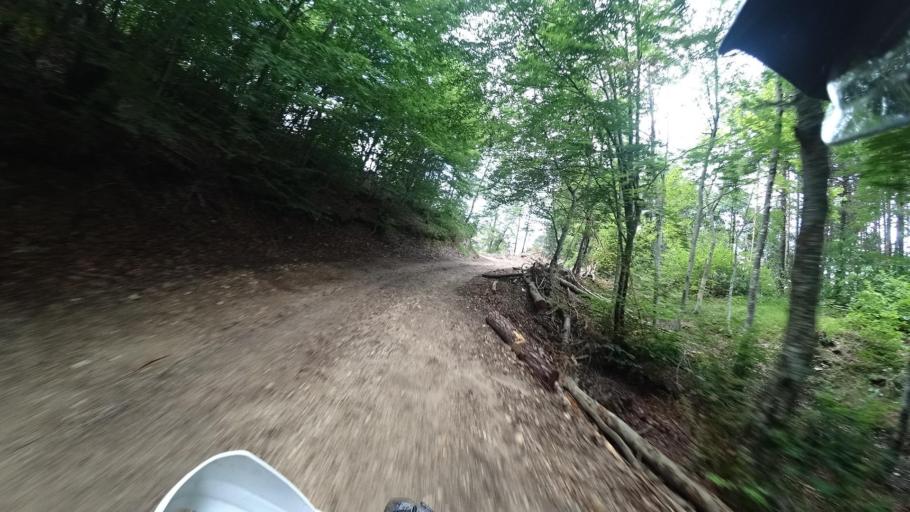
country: HR
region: Licko-Senjska
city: Otocac
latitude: 44.8734
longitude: 15.4077
